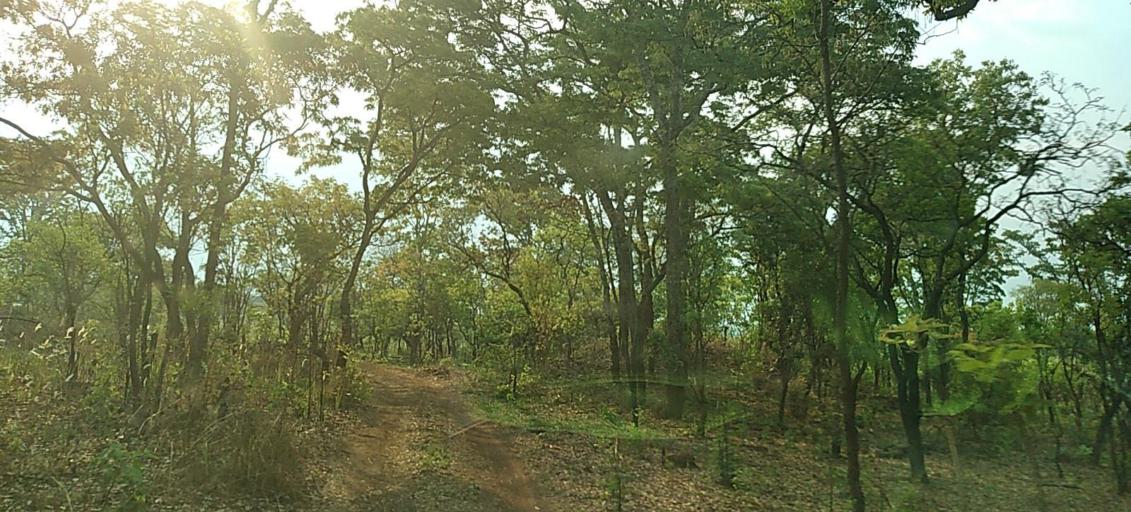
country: ZM
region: North-Western
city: Solwezi
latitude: -12.0423
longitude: 26.0457
